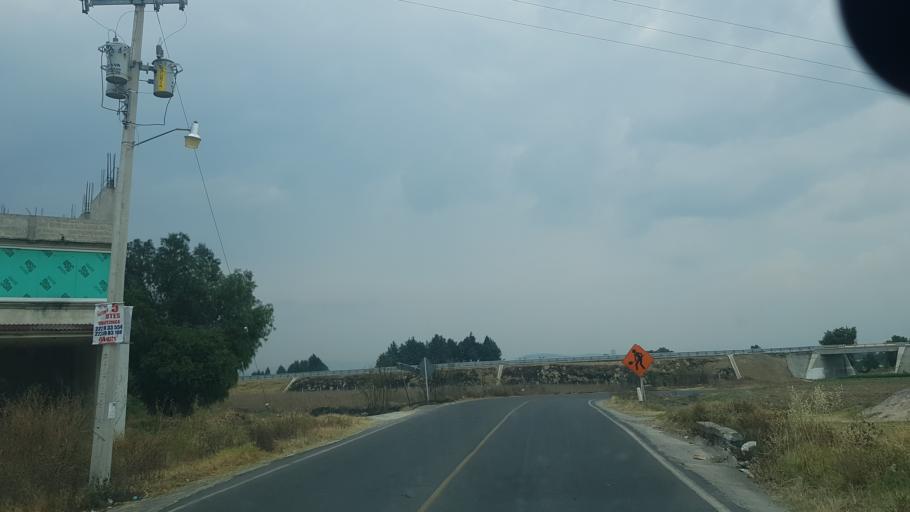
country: MX
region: Puebla
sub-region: Huejotzingo
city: San Mateo Capultitlan
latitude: 19.2035
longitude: -98.4317
